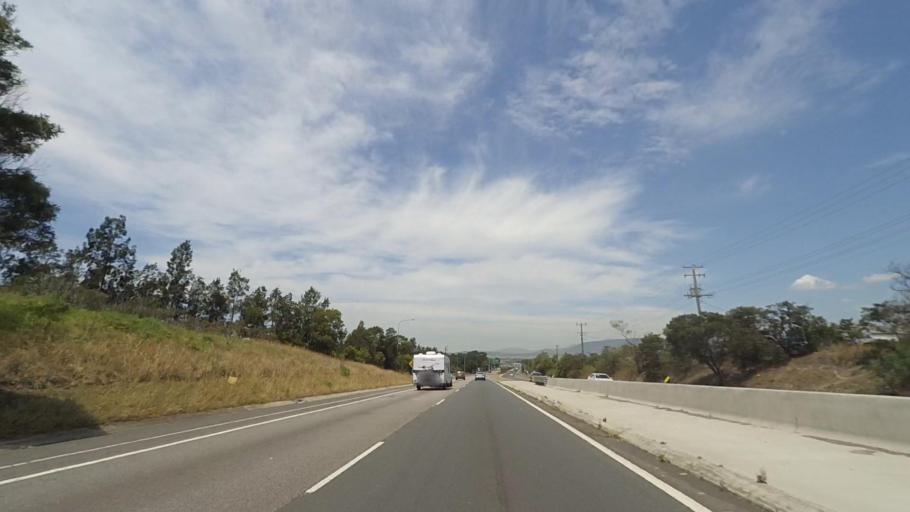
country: AU
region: New South Wales
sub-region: Shellharbour
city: Albion Park Rail
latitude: -34.5421
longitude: 150.7849
